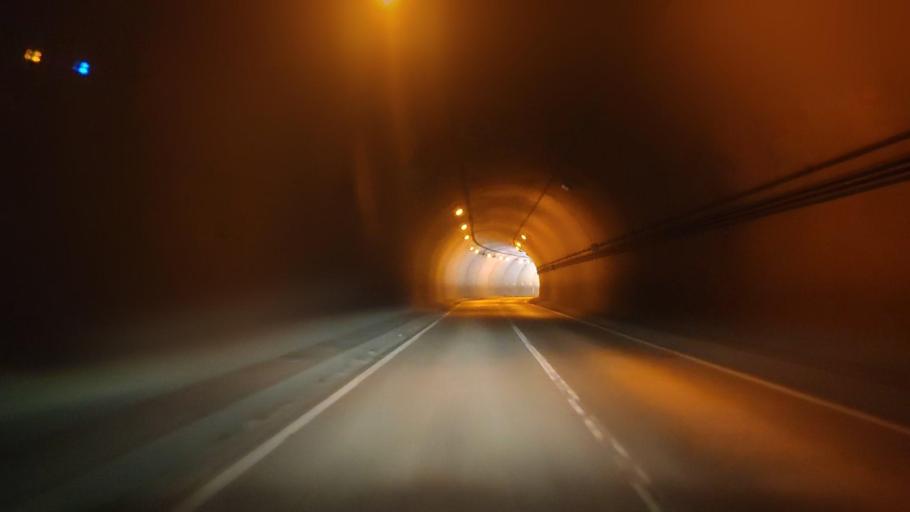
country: JP
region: Kumamoto
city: Hitoyoshi
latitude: 32.4143
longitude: 130.8439
